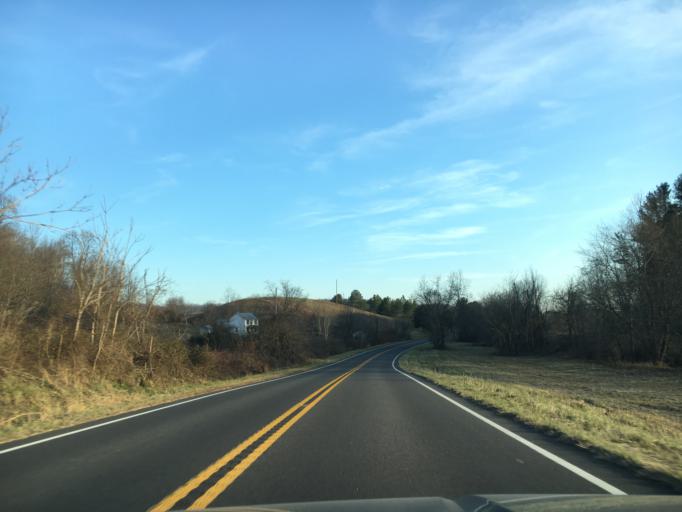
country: US
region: Virginia
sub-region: Rappahannock County
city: Washington
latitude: 38.6301
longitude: -78.1892
